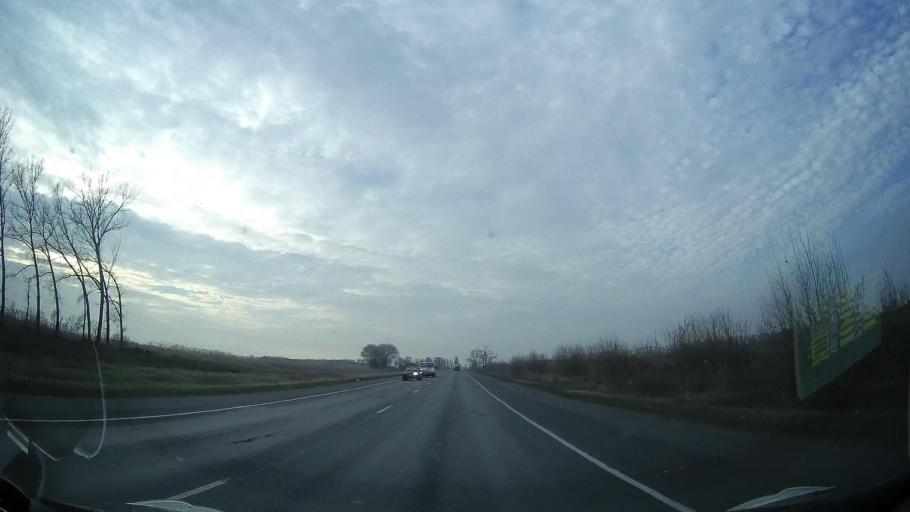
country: RU
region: Rostov
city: Starocherkasskaya
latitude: 47.1547
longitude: 40.1736
